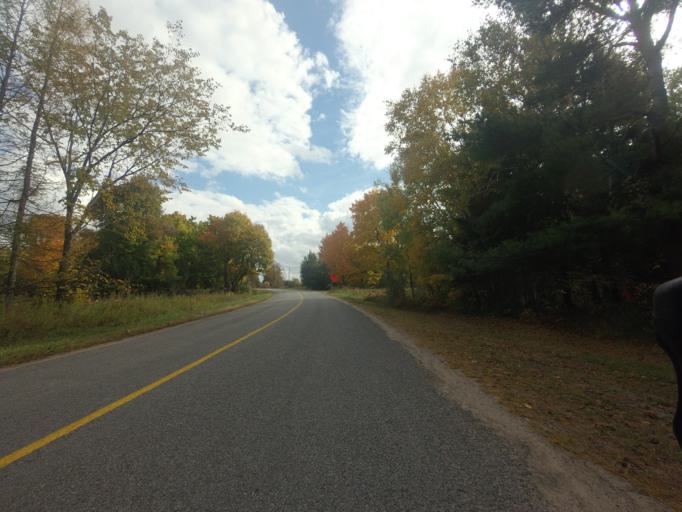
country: CA
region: Ontario
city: Pembroke
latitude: 45.5712
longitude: -77.1268
